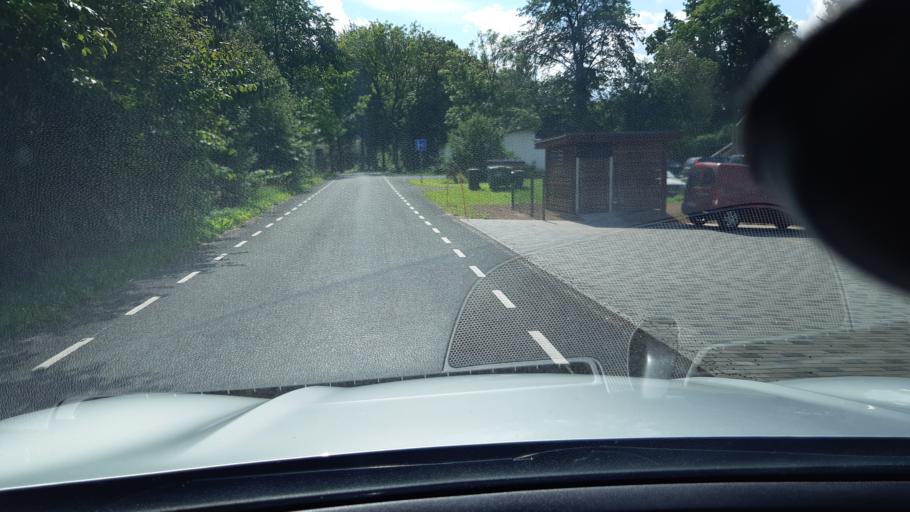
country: EE
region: Raplamaa
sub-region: Kehtna vald
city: Kehtna
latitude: 58.9407
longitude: 24.8981
